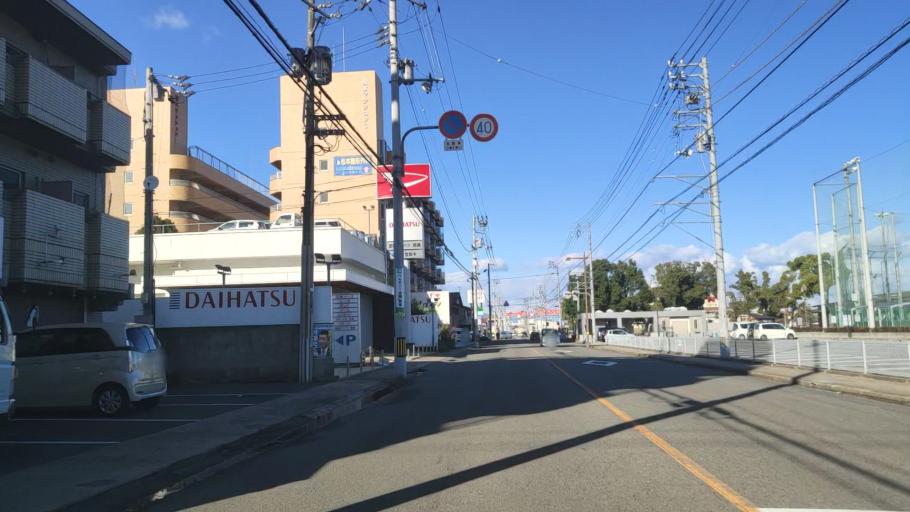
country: JP
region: Ehime
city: Saijo
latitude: 33.9162
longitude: 133.1920
